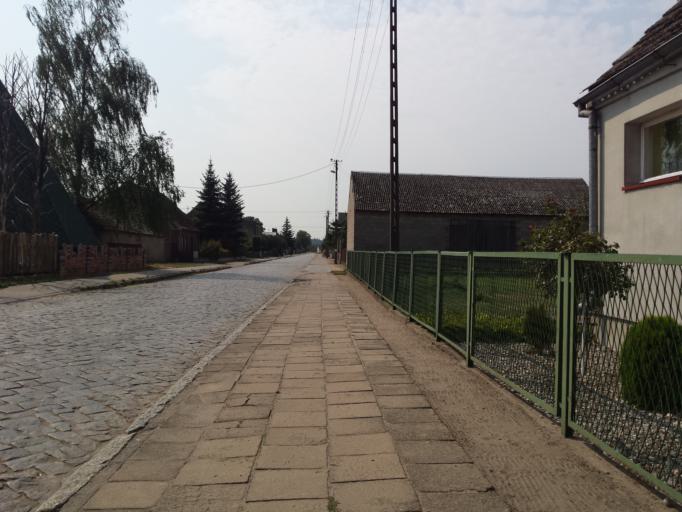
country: PL
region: Greater Poland Voivodeship
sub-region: Powiat czarnkowsko-trzcianecki
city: Polajewo
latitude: 52.7713
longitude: 16.6404
